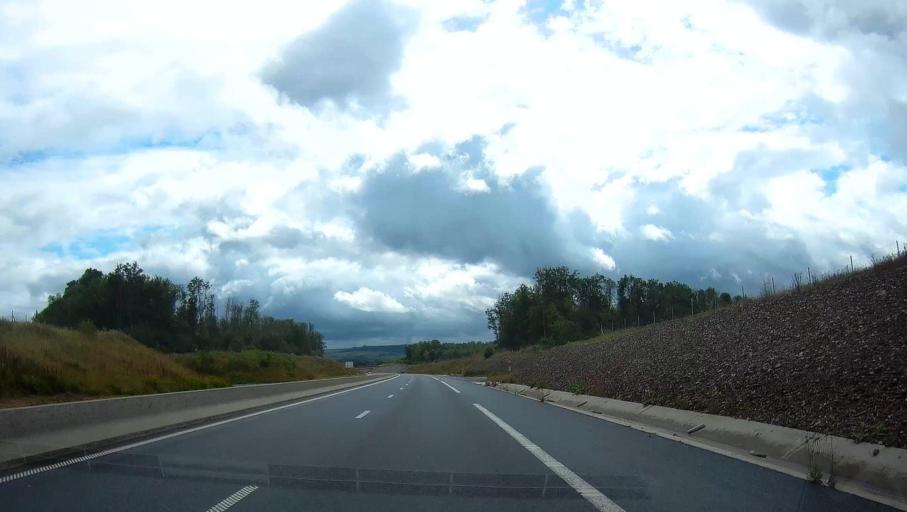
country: FR
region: Champagne-Ardenne
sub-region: Departement des Ardennes
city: Rimogne
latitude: 49.8220
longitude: 4.5132
